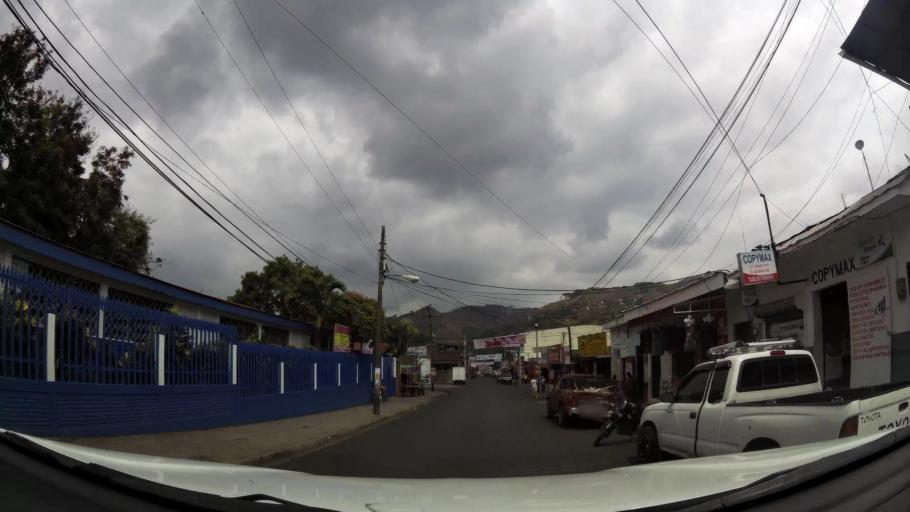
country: NI
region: Matagalpa
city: Matagalpa
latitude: 12.9215
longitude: -85.9207
